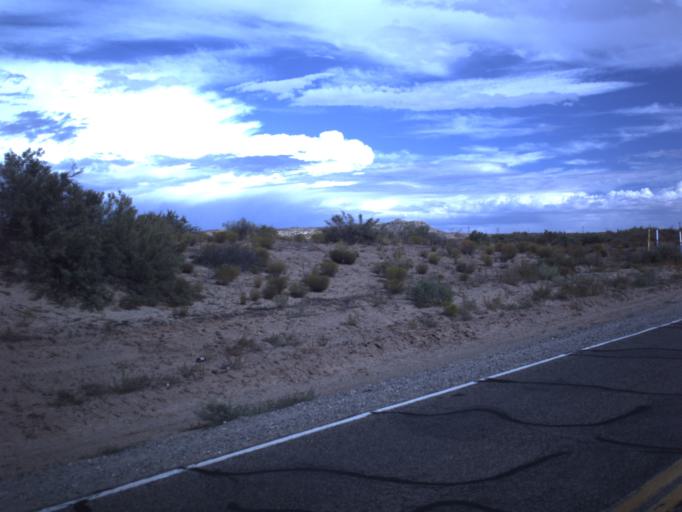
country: US
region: Utah
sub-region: San Juan County
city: Blanding
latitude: 37.2525
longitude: -109.2575
